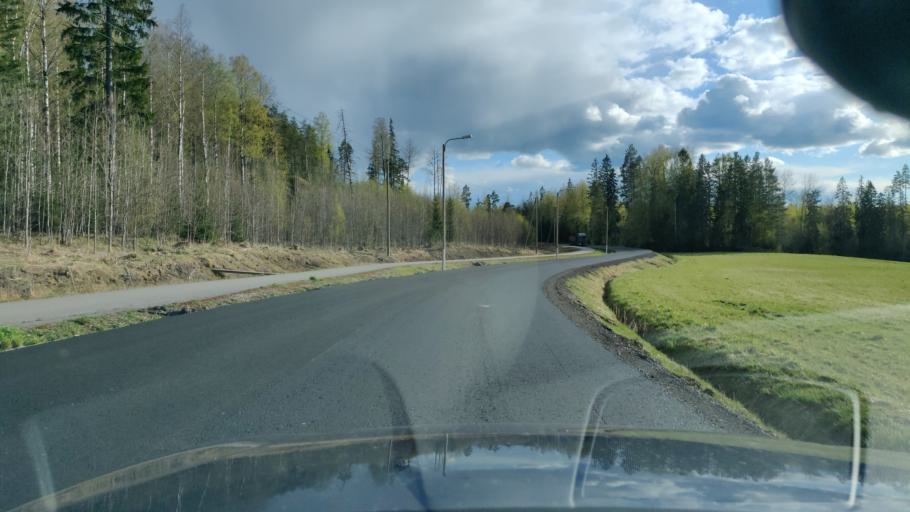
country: FI
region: Uusimaa
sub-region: Helsinki
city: Nurmijaervi
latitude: 60.3666
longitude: 24.7285
